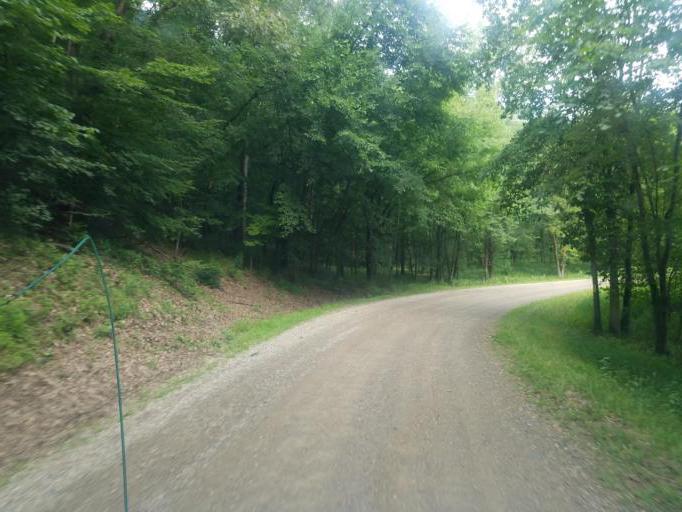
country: US
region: Ohio
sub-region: Knox County
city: Oak Hill
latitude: 40.4022
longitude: -82.1683
